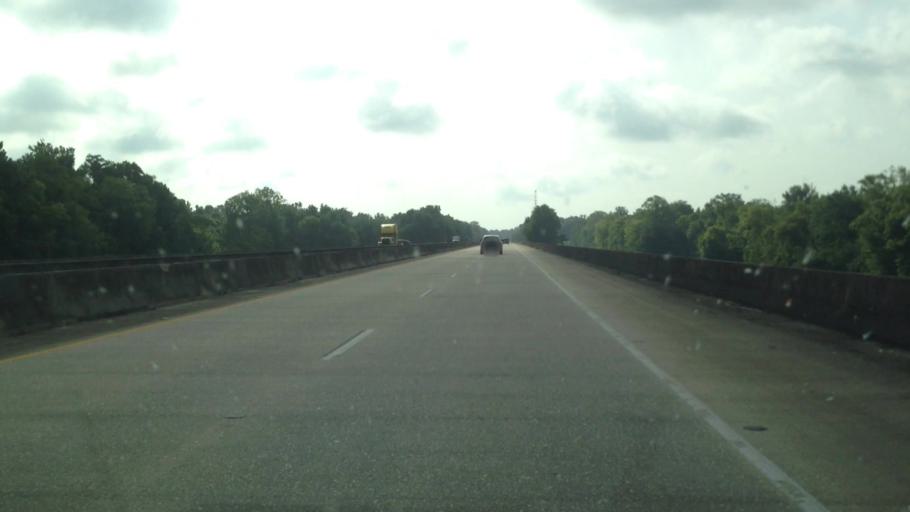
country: US
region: Louisiana
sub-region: Saint Landry Parish
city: Krotz Springs
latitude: 30.5415
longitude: -91.7855
